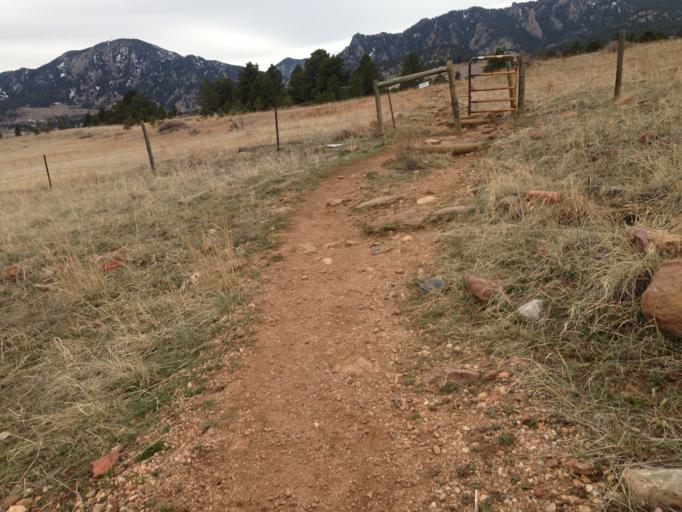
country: US
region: Colorado
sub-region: Boulder County
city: Boulder
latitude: 39.9495
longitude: -105.2521
